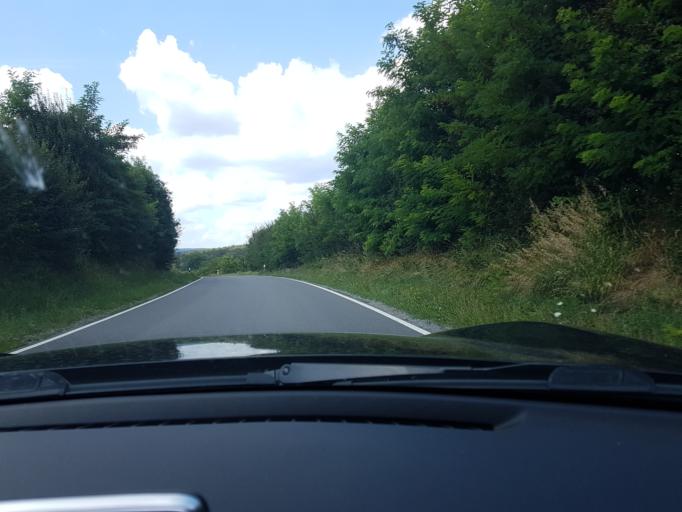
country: DE
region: Baden-Wuerttemberg
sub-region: Karlsruhe Region
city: Limbach
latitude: 49.4222
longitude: 9.2616
